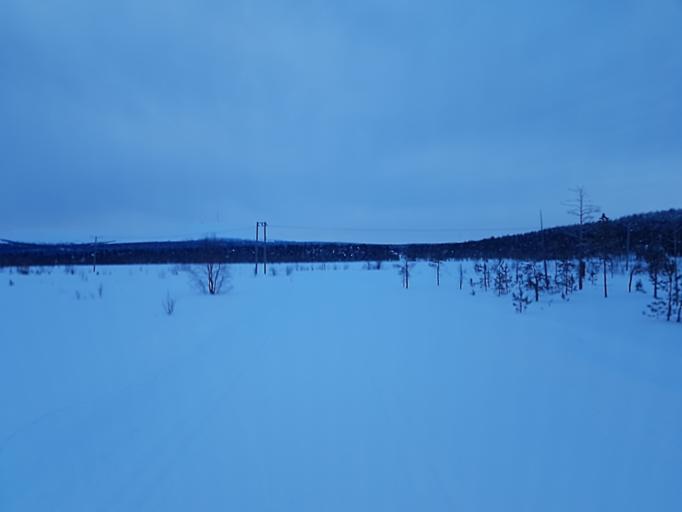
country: FI
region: Lapland
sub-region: Tunturi-Lappi
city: Kolari
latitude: 67.6175
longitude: 24.1316
